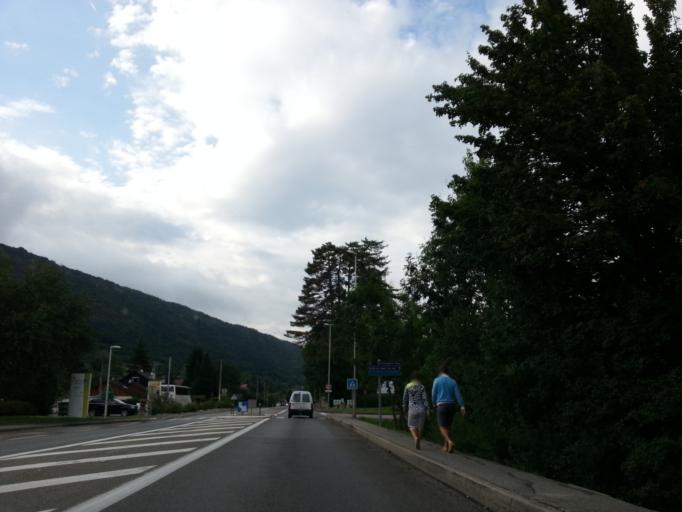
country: FR
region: Rhone-Alpes
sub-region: Departement de la Haute-Savoie
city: Sevrier
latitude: 45.8542
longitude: 6.1440
